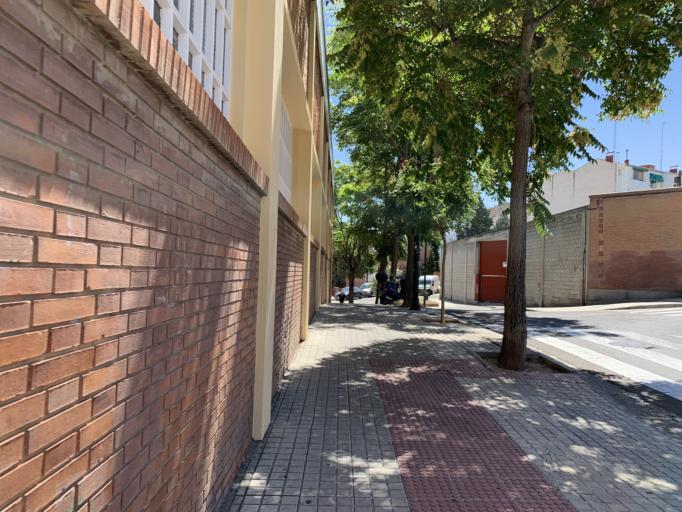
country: ES
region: Aragon
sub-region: Provincia de Zaragoza
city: Zaragoza
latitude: 41.6371
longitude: -0.8815
